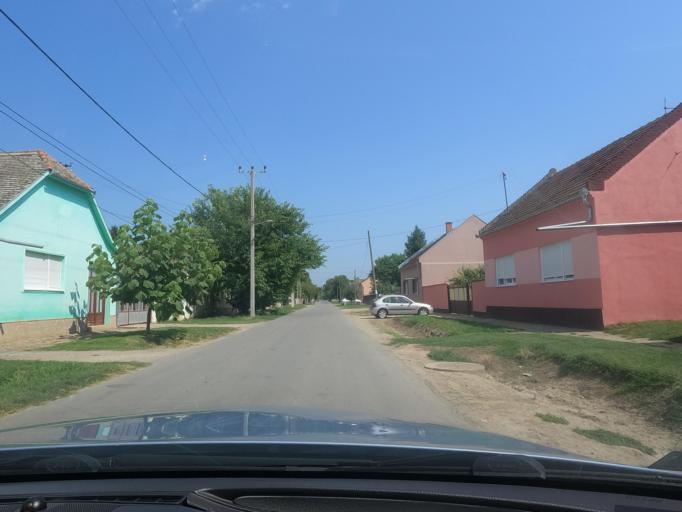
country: RS
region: Autonomna Pokrajina Vojvodina
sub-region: Juznobacki Okrug
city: Kovilj
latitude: 45.2235
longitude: 20.0248
